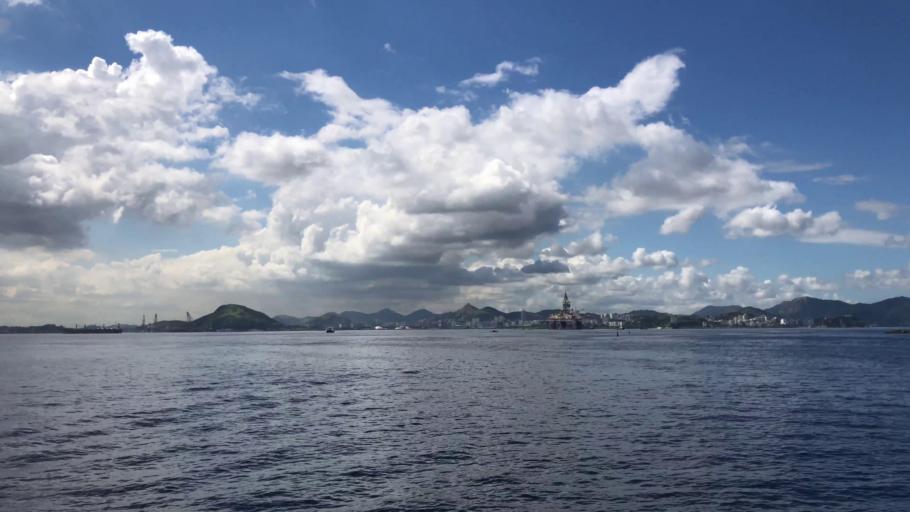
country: BR
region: Rio de Janeiro
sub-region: Rio De Janeiro
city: Rio de Janeiro
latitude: -22.9012
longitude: -43.1647
